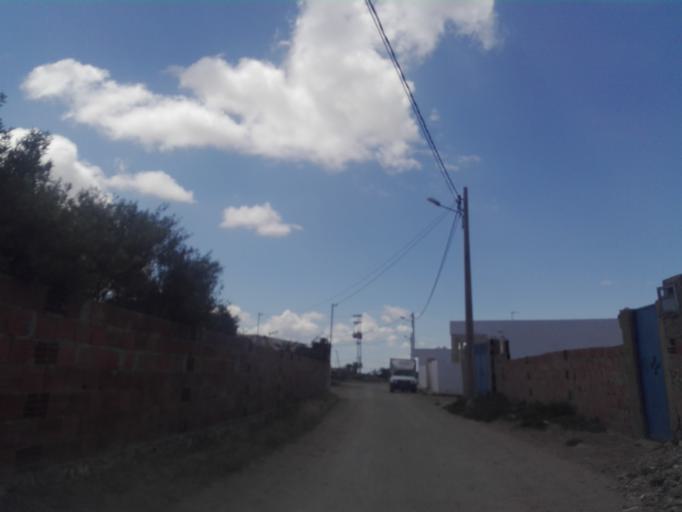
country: TN
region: Safaqis
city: Jabinyanah
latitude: 34.8207
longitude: 11.2528
